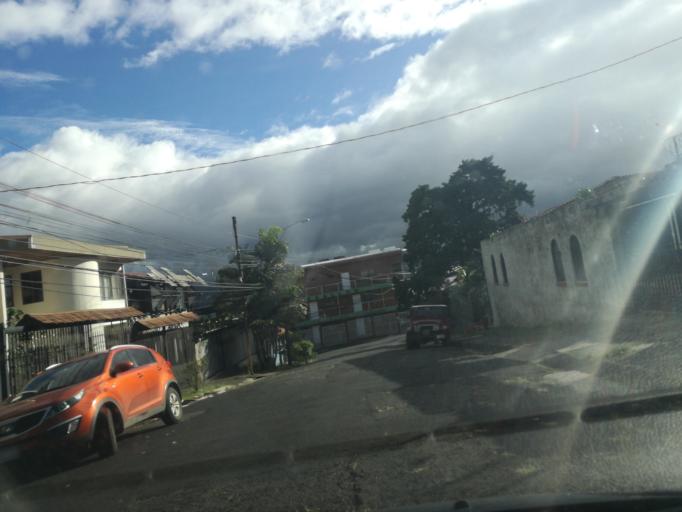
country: CR
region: San Jose
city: San Pedro
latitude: 9.9290
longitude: -84.0517
